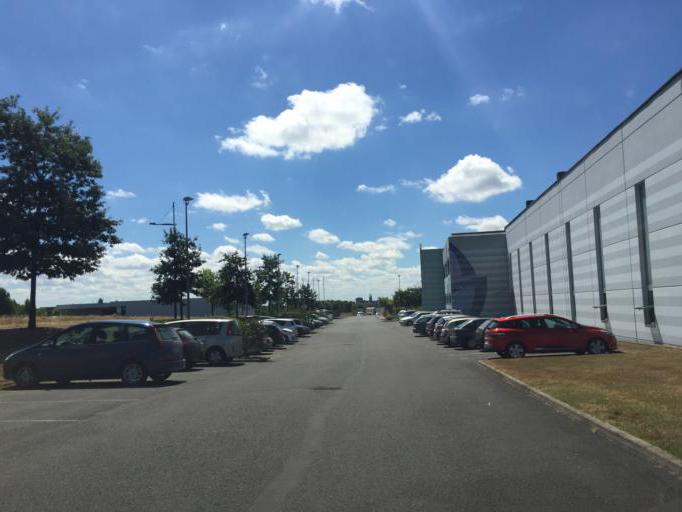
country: FR
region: Auvergne
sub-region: Departement de l'Allier
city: Avermes
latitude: 46.5958
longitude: 3.3283
